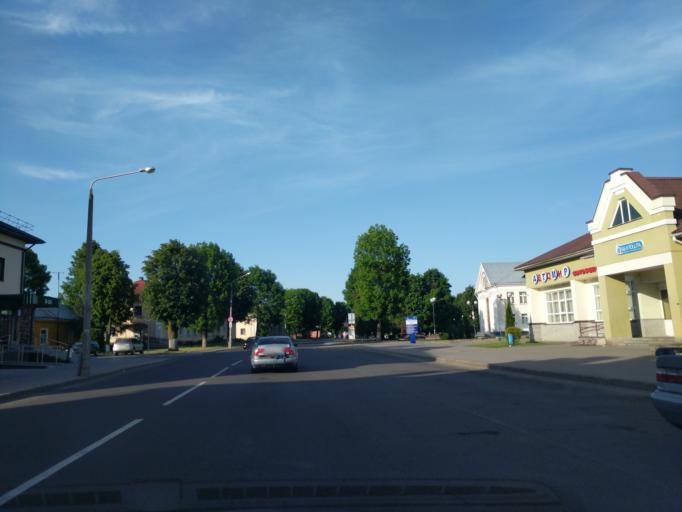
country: BY
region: Grodnenskaya
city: Ashmyany
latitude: 54.4261
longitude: 25.9381
